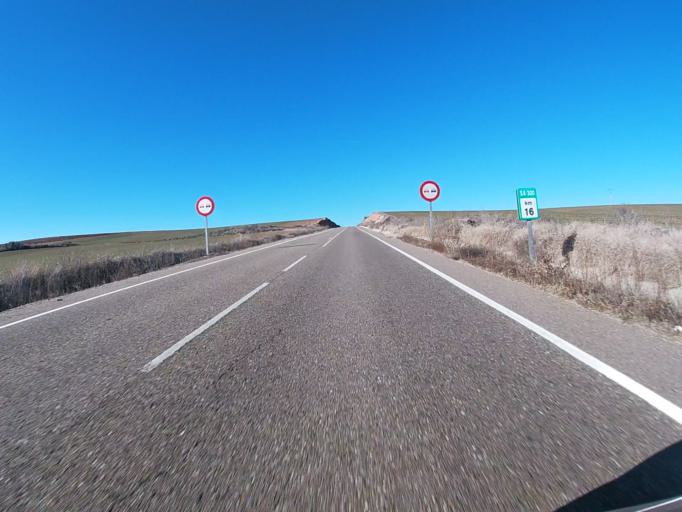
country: ES
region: Castille and Leon
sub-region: Provincia de Salamanca
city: Almenara de Tormes
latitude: 41.0702
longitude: -5.8292
